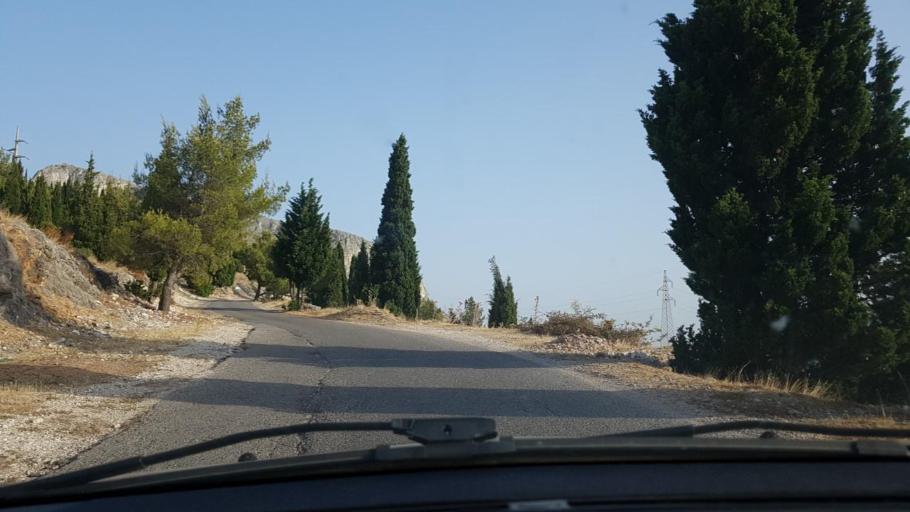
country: BA
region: Federation of Bosnia and Herzegovina
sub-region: Hercegovacko-Bosanski Kanton
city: Mostar
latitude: 43.3517
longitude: 17.8213
